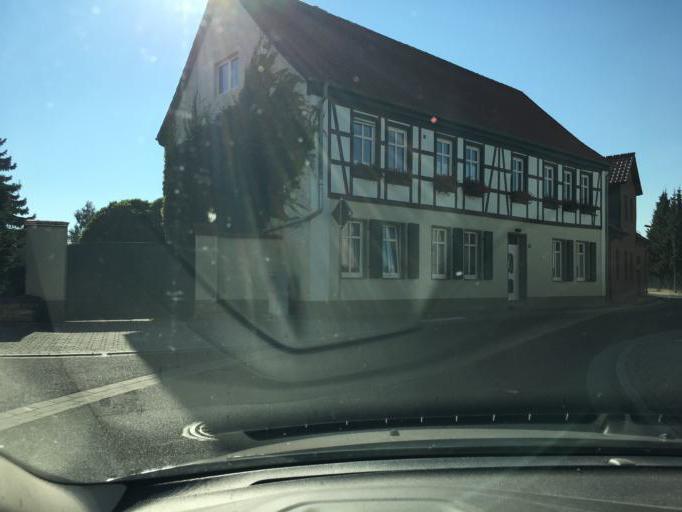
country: DE
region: Saxony-Anhalt
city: Wanzleben
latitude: 52.0589
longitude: 11.4383
